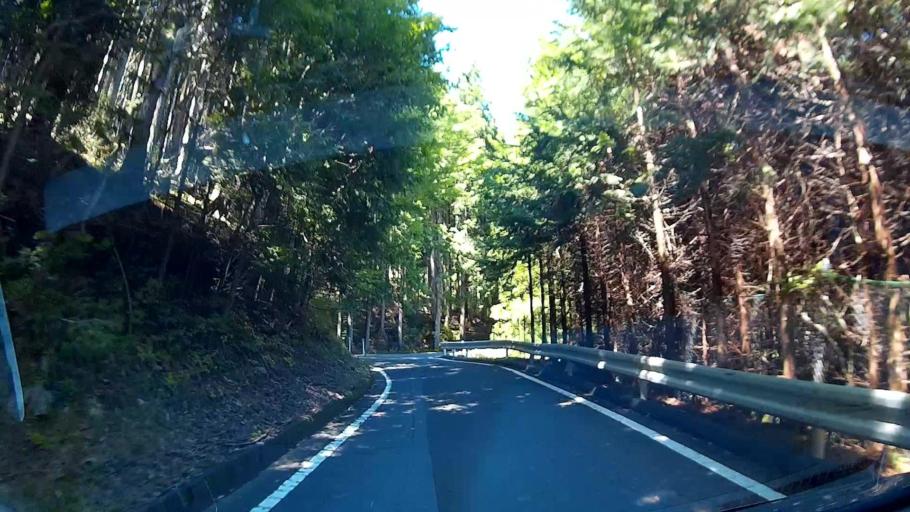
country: JP
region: Shizuoka
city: Shizuoka-shi
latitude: 35.1939
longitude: 138.2593
